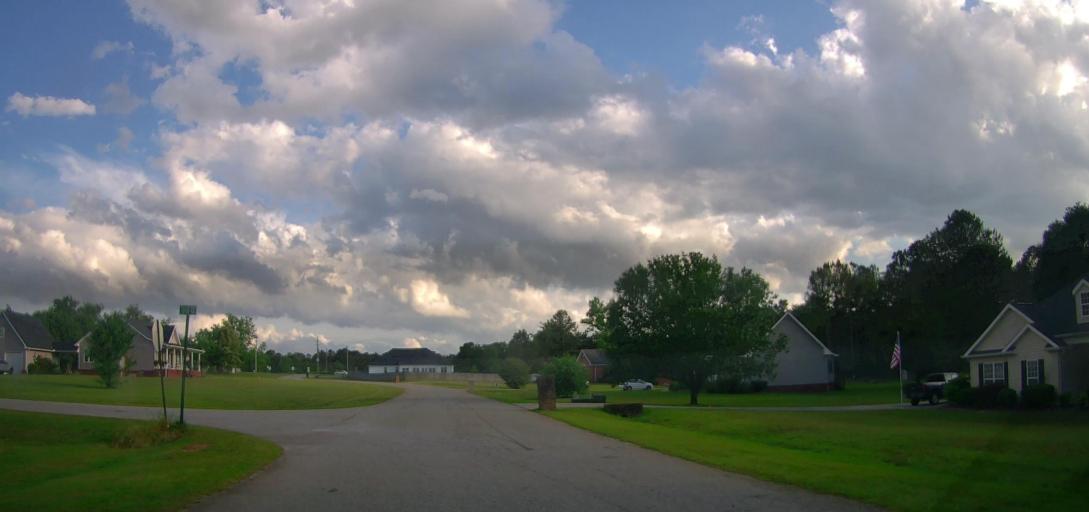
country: US
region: Georgia
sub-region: Peach County
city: Byron
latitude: 32.6207
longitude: -83.7714
